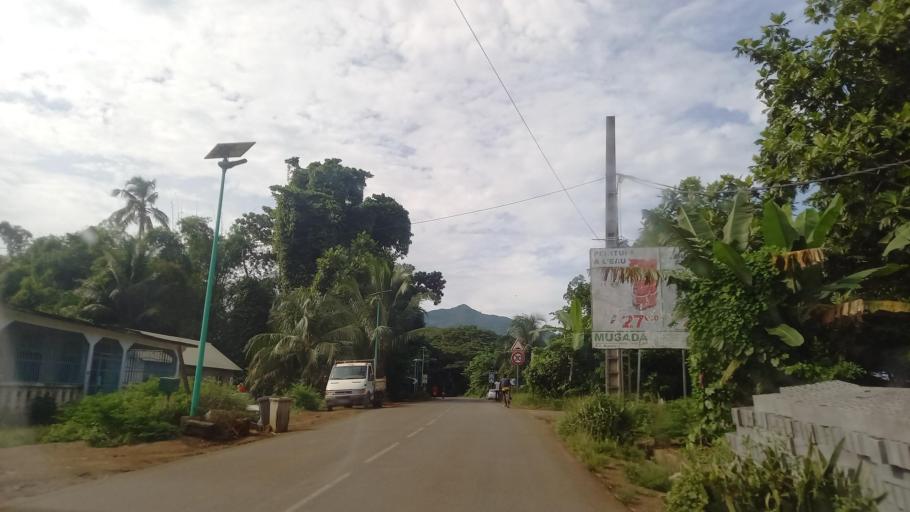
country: YT
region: Chirongui
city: Chirongui
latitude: -12.9195
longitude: 45.1590
